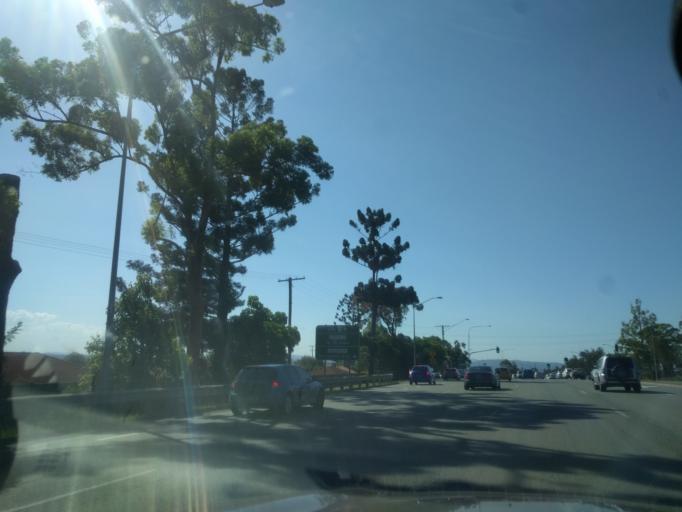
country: AU
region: Queensland
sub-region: Brisbane
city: Sunnybank Hills
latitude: -27.6001
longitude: 153.0405
